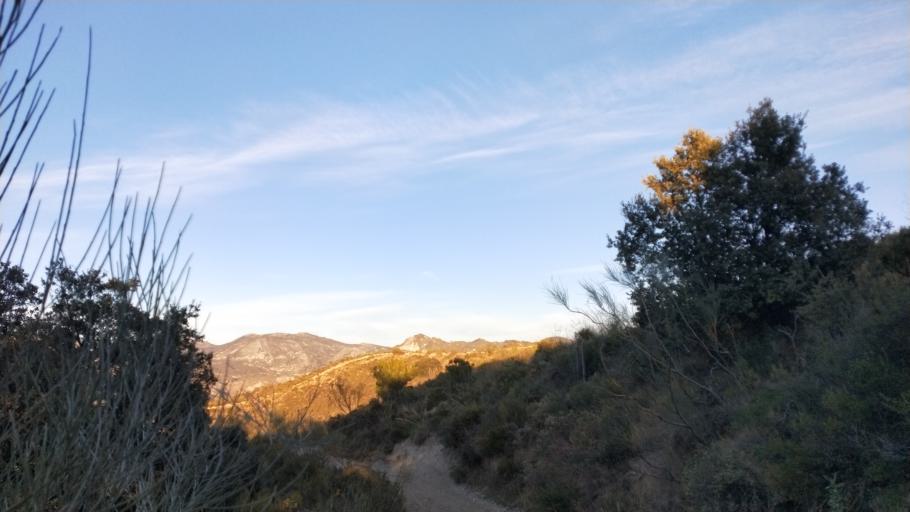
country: ES
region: Andalusia
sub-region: Provincia de Granada
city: Huetor Santillan
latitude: 37.2042
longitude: -3.5015
